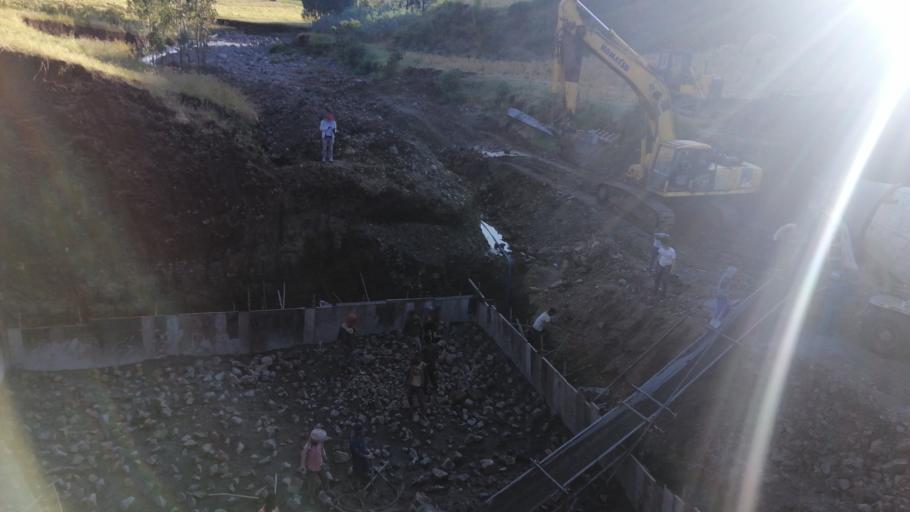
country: ET
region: Amhara
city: Debre Tabor
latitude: 11.5211
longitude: 38.1719
